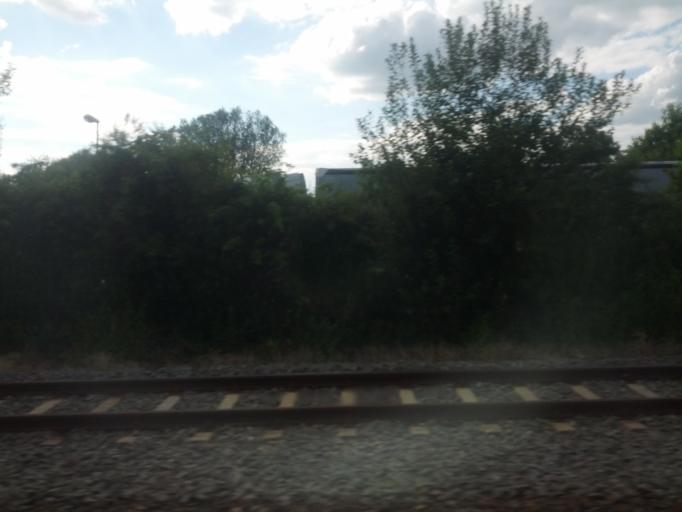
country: DE
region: Baden-Wuerttemberg
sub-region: Karlsruhe Region
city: Weingarten
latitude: 49.0521
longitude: 8.5145
